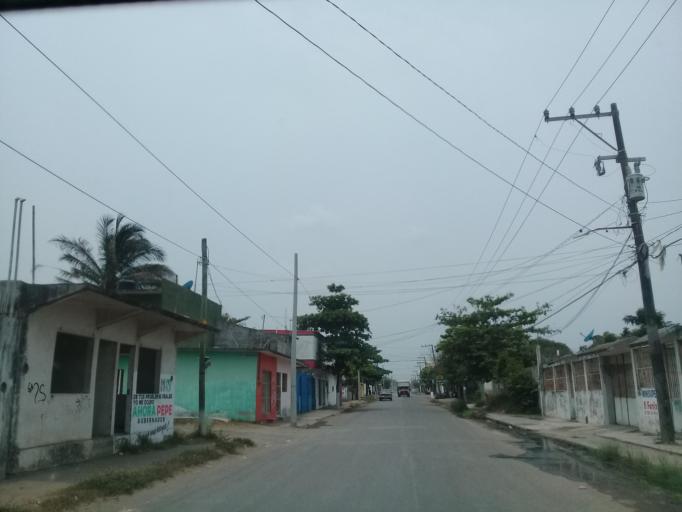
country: MX
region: Veracruz
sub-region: Veracruz
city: Las Amapolas
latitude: 19.1468
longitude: -96.2012
